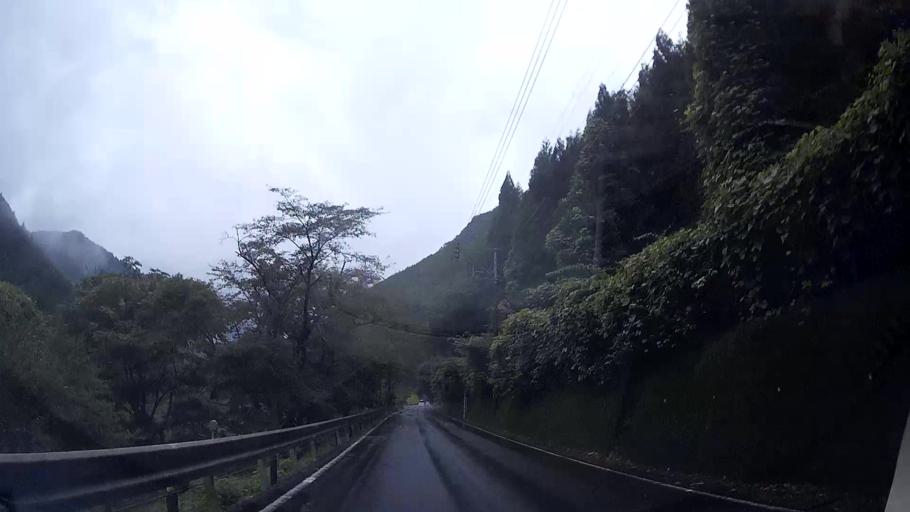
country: JP
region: Oita
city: Hita
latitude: 33.1783
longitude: 131.0142
